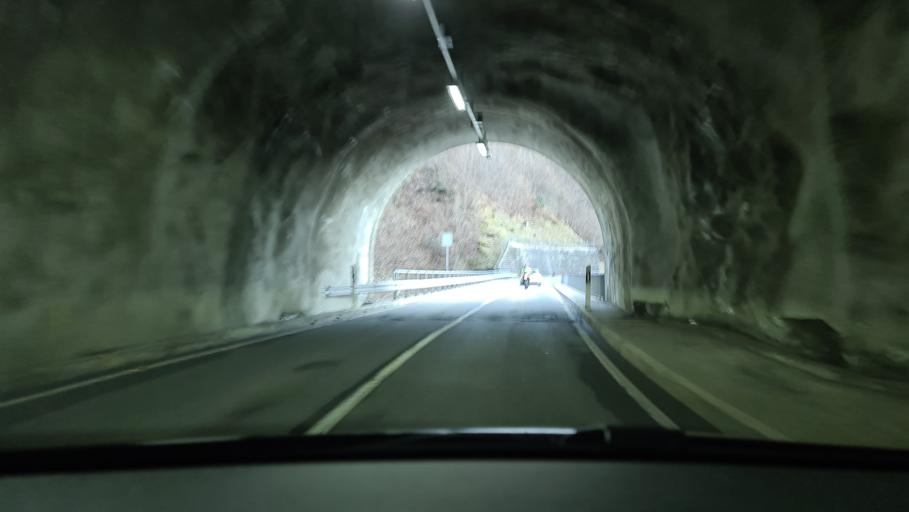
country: CH
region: Ticino
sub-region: Locarno District
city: Gordola
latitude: 46.2099
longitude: 8.8600
